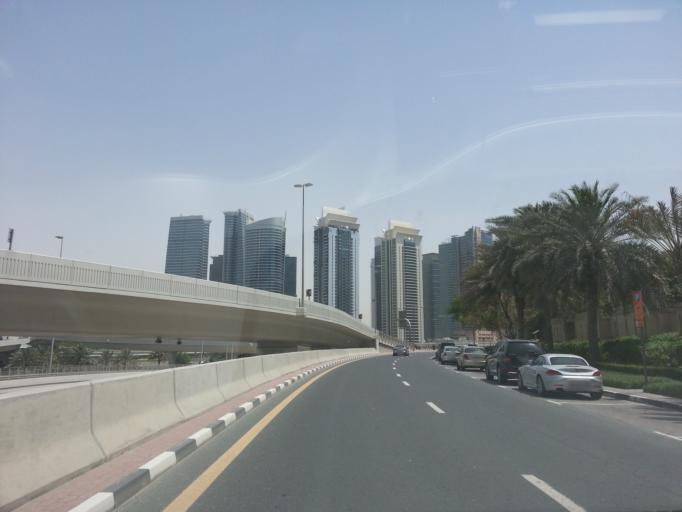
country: AE
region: Dubai
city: Dubai
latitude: 25.0861
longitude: 55.1501
